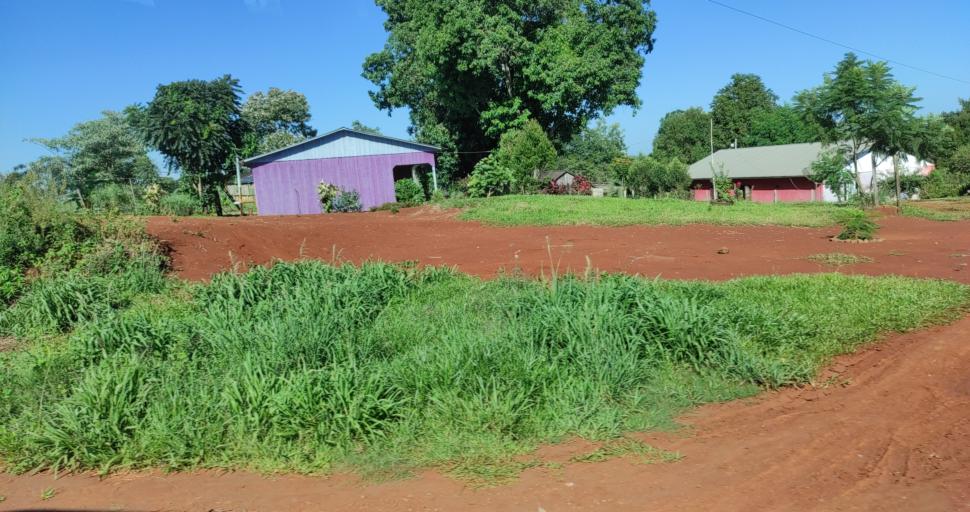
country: AR
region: Misiones
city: El Soberbio
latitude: -27.1879
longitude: -54.1062
